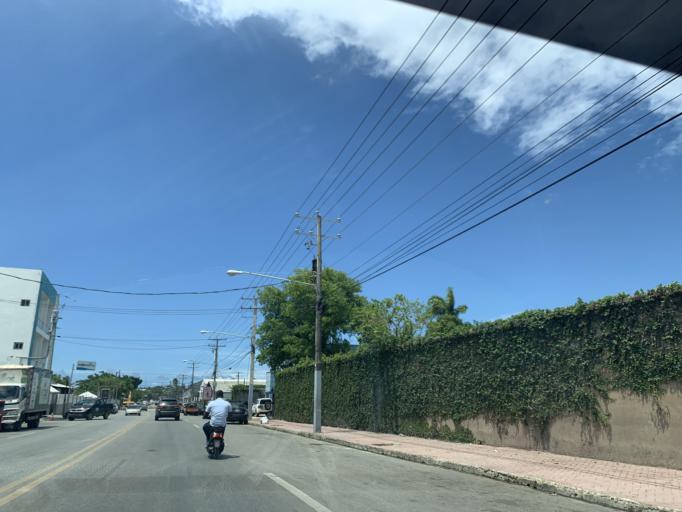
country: DO
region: Puerto Plata
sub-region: Puerto Plata
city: Puerto Plata
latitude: 19.7931
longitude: -70.6996
